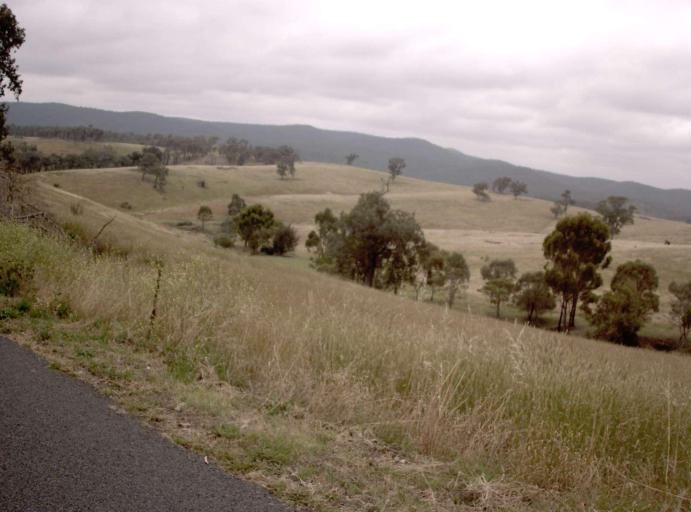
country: AU
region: Victoria
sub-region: Wellington
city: Heyfield
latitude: -37.8672
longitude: 146.7068
